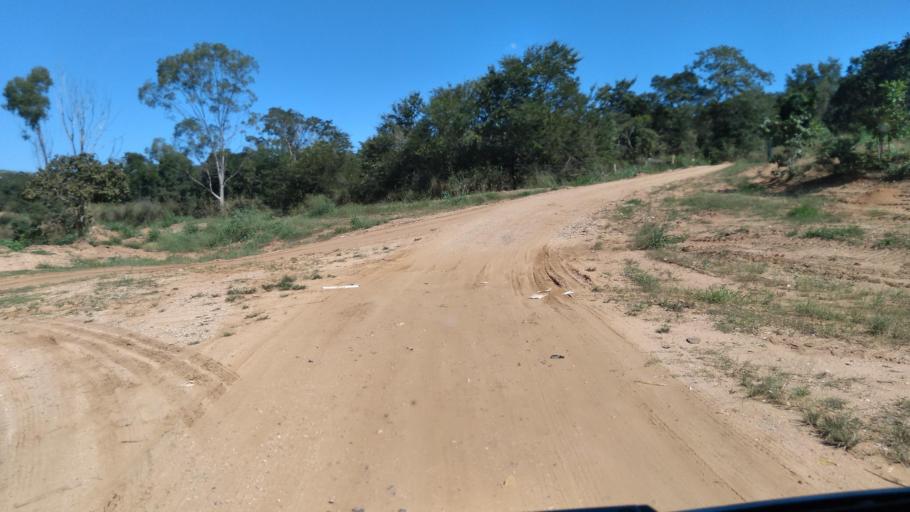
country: BR
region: Goias
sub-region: Mineiros
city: Mineiros
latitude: -17.5973
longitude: -52.4976
